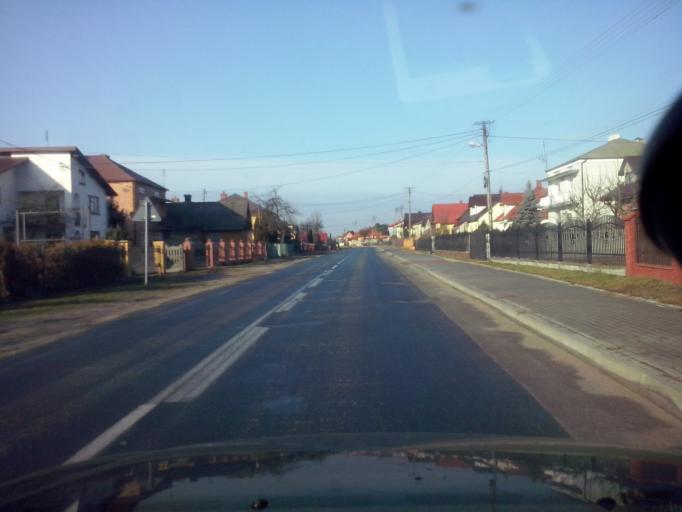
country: PL
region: Subcarpathian Voivodeship
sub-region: Powiat lezajski
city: Letownia
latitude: 50.3656
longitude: 22.2224
